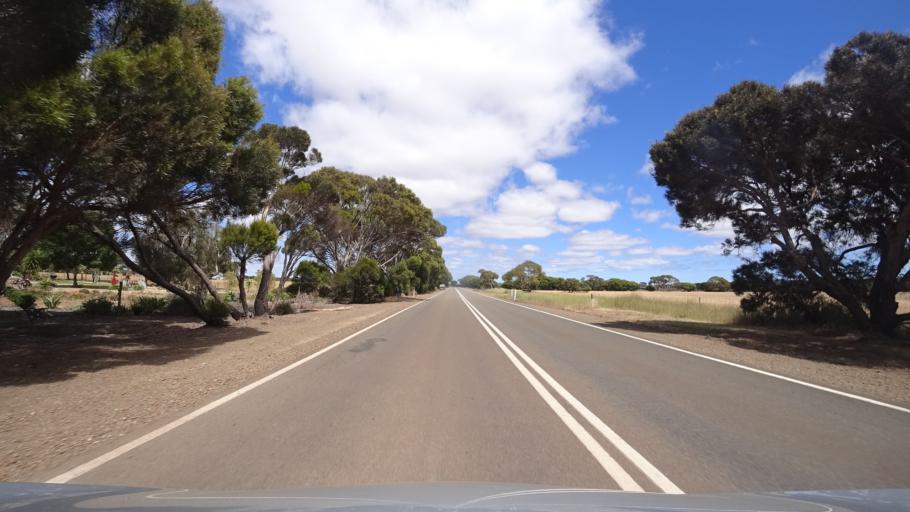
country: AU
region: South Australia
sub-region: Kangaroo Island
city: Kingscote
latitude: -35.6814
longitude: 137.5576
